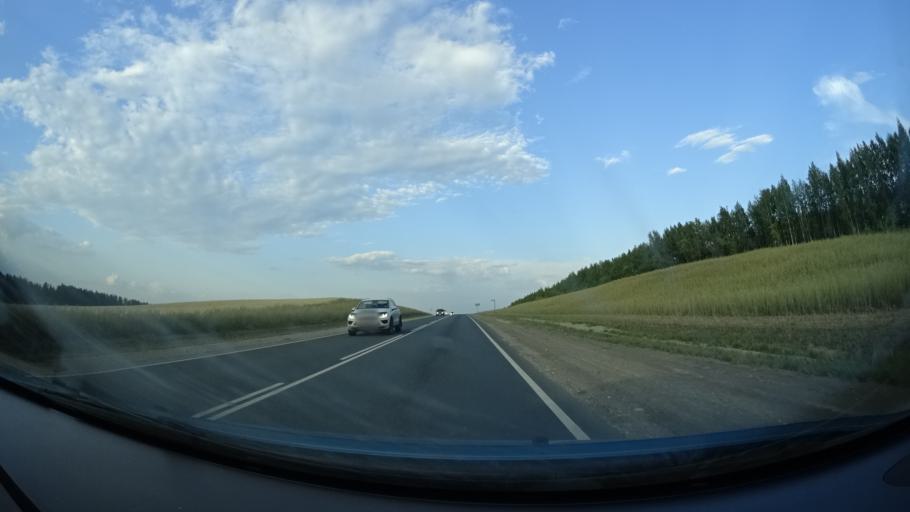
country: RU
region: Samara
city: Isakly
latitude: 54.0195
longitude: 51.8061
